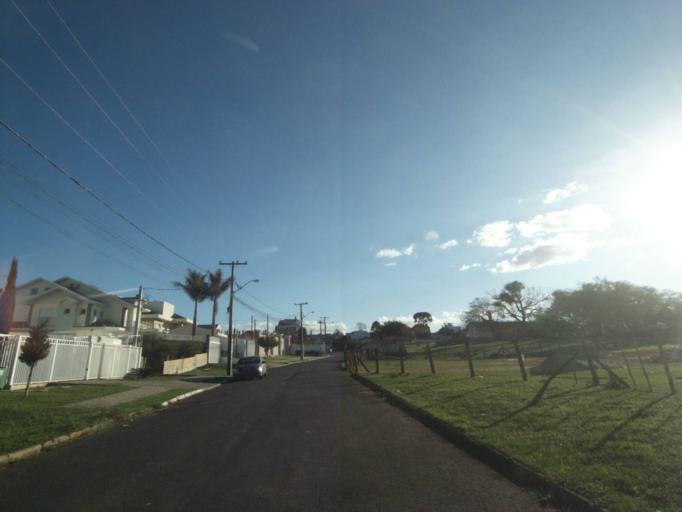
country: BR
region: Parana
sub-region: Curitiba
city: Curitiba
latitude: -25.3854
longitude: -49.2453
